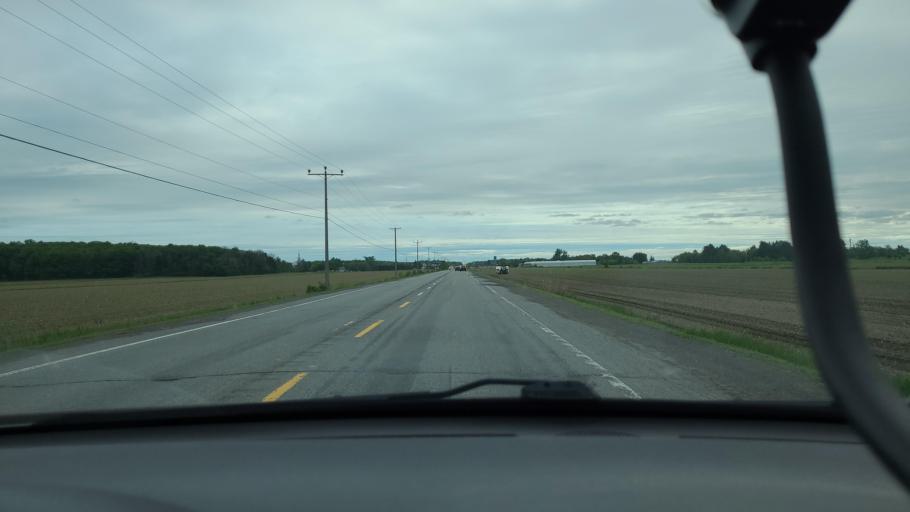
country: CA
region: Quebec
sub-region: Lanaudiere
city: Saint-Jacques
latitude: 45.9240
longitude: -73.6224
